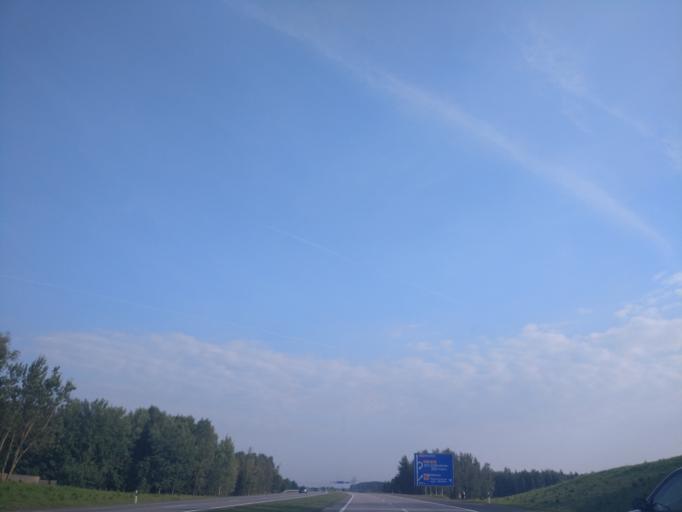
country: BY
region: Minsk
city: Astrashytski Haradok
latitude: 54.0459
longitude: 27.7009
